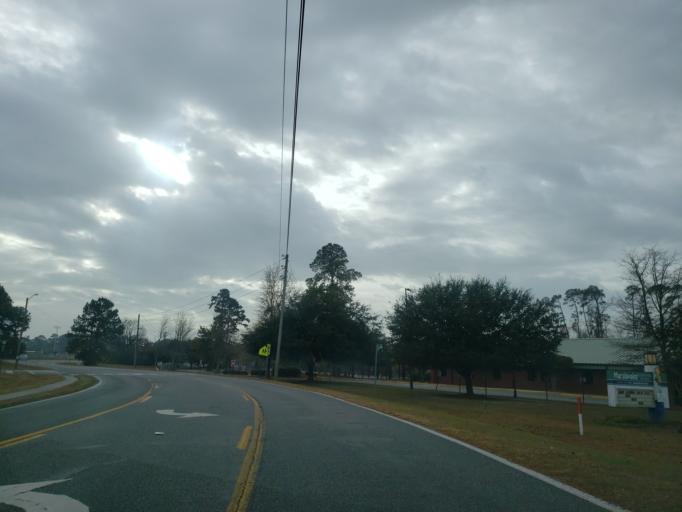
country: US
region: Georgia
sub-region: Chatham County
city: Whitemarsh Island
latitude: 32.0407
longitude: -81.0099
